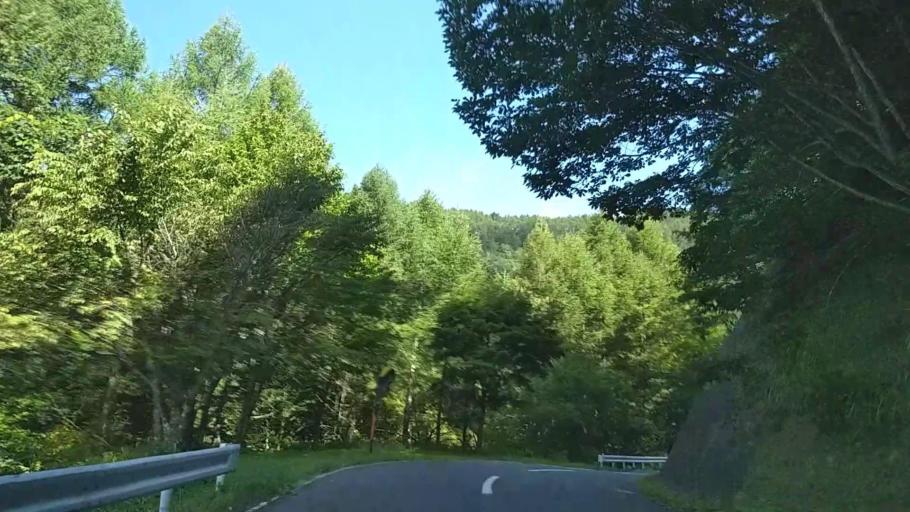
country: JP
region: Nagano
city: Matsumoto
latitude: 36.1970
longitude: 138.1146
